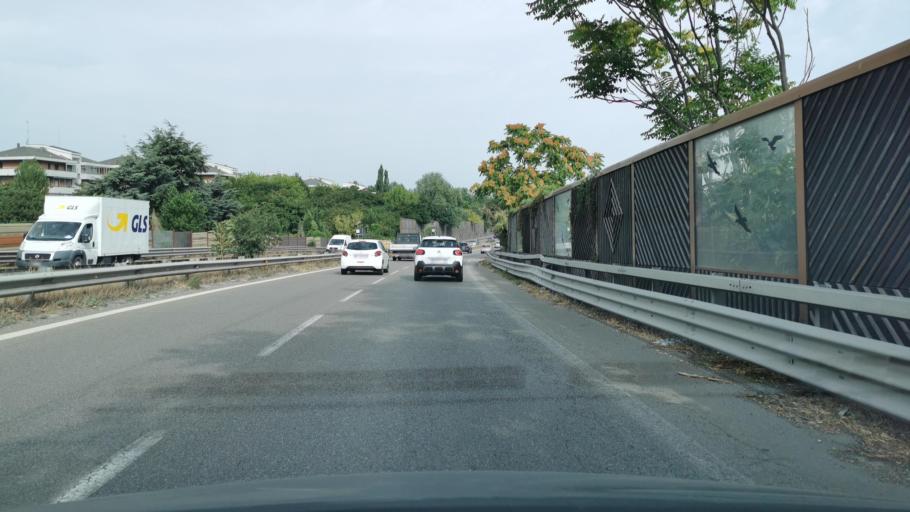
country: IT
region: Emilia-Romagna
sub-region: Provincia di Modena
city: Modena
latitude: 44.6605
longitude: 10.9456
